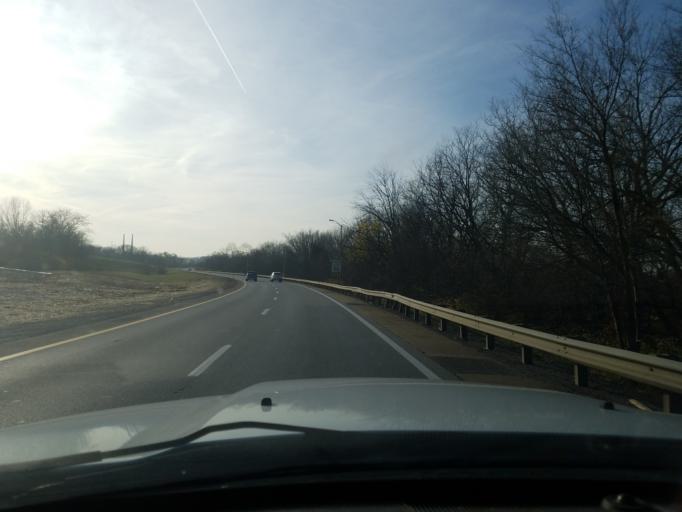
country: US
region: Indiana
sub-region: Floyd County
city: New Albany
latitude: 38.2772
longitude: -85.8080
